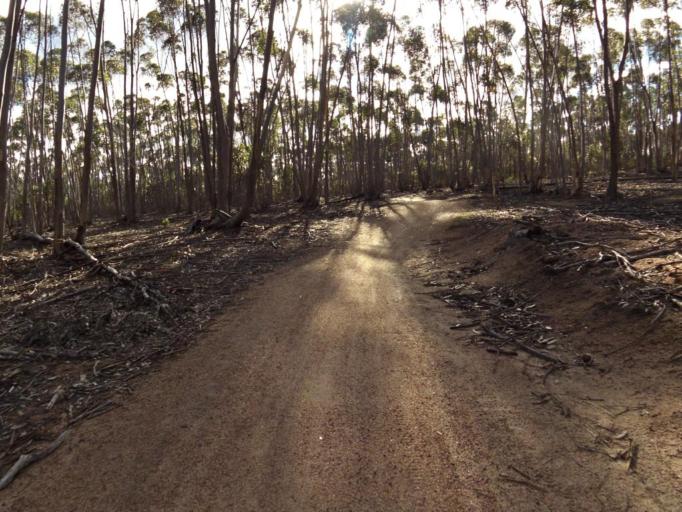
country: AU
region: Victoria
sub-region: Greater Geelong
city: Lara
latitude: -37.9445
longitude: 144.4094
